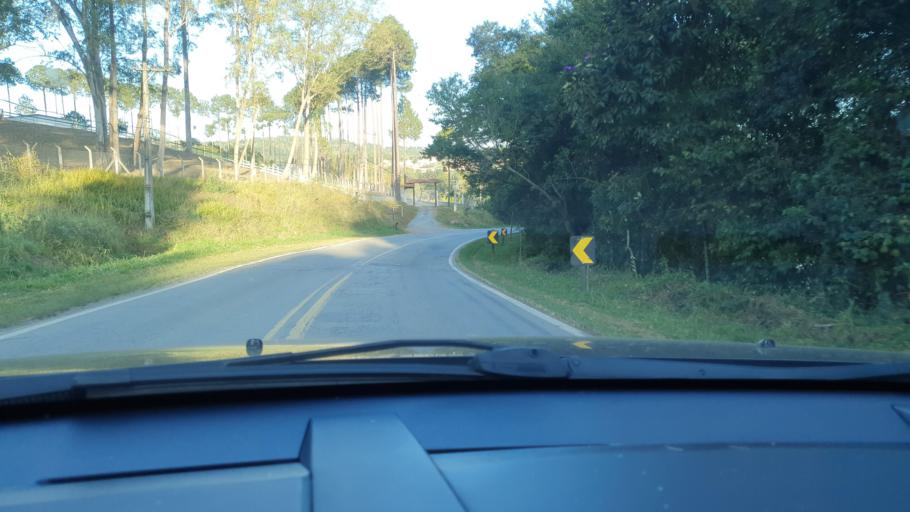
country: BR
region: Sao Paulo
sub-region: Piedade
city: Piedade
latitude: -23.6782
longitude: -47.3357
